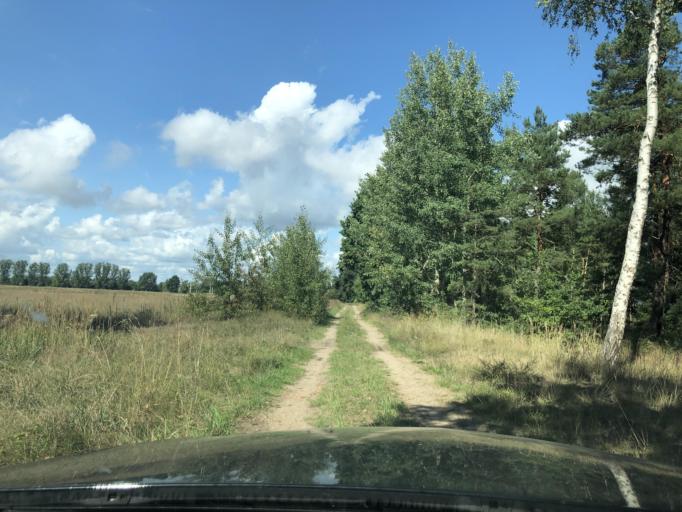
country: DE
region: Brandenburg
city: Luebben
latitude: 51.9549
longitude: 13.8363
